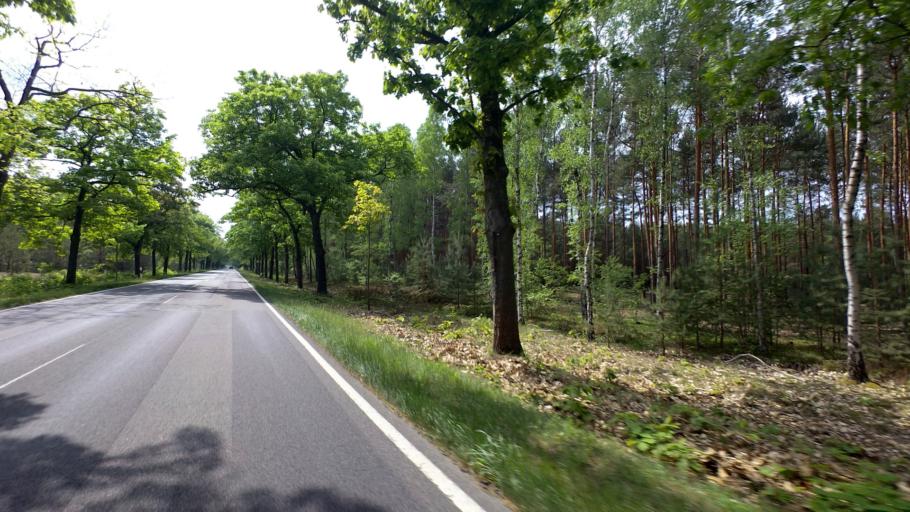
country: DE
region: Brandenburg
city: Drachhausen
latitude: 51.9273
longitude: 14.3461
